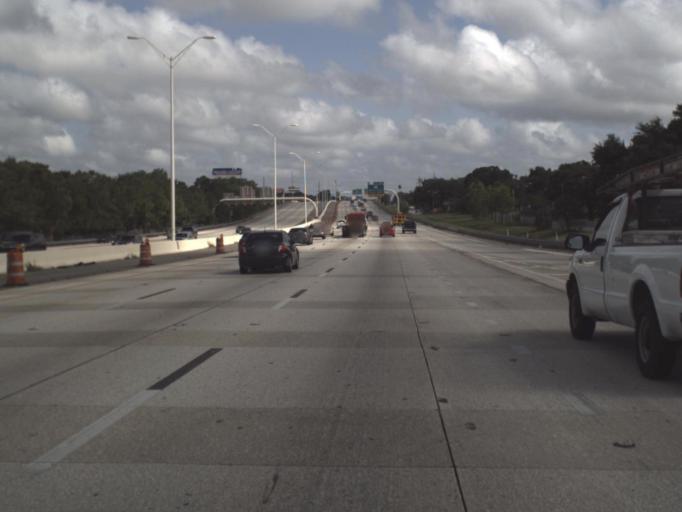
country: US
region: Florida
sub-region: Hillsborough County
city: Tampa
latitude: 27.9725
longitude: -82.4533
